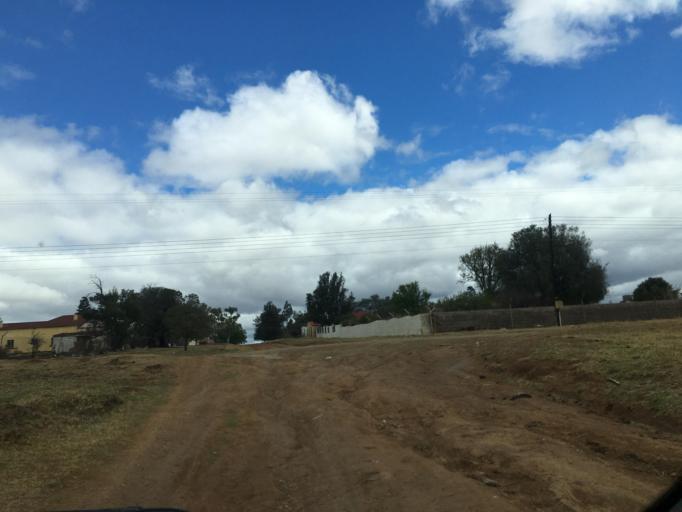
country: ZA
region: Eastern Cape
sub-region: Chris Hani District Municipality
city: Cala
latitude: -31.5230
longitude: 27.7022
